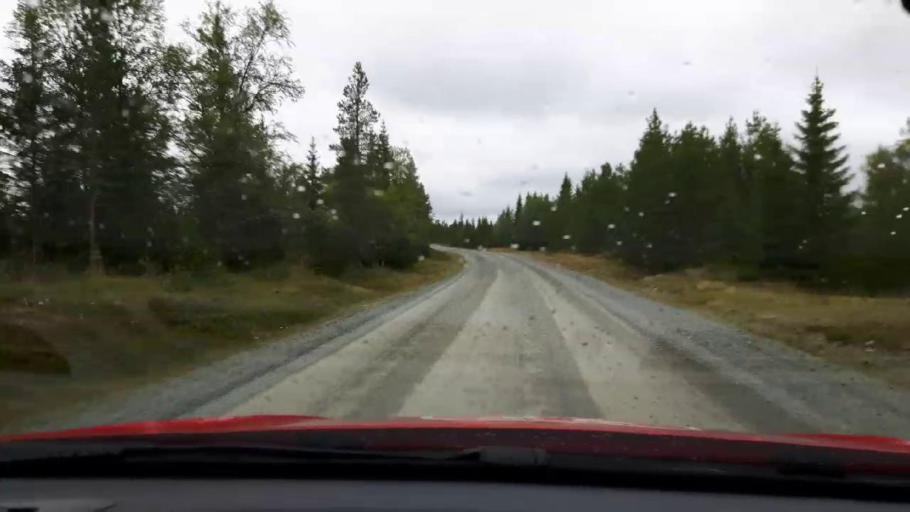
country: SE
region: Jaemtland
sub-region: Bergs Kommun
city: Hoverberg
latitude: 62.9009
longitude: 14.0594
